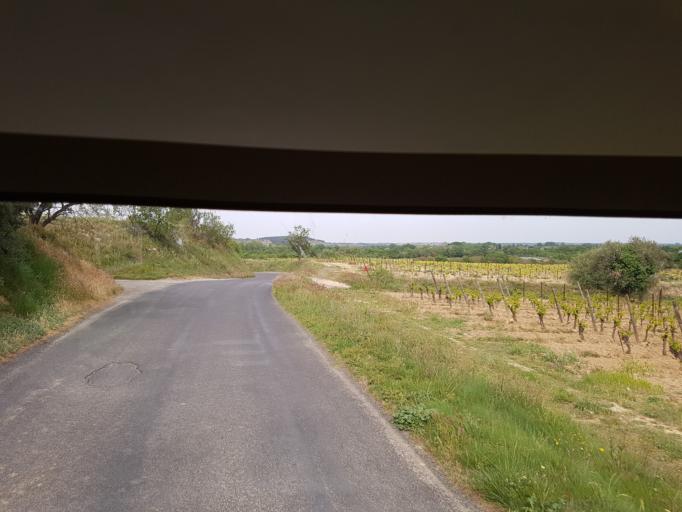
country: FR
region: Languedoc-Roussillon
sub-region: Departement de l'Aude
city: Fleury
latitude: 43.2382
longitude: 3.1455
